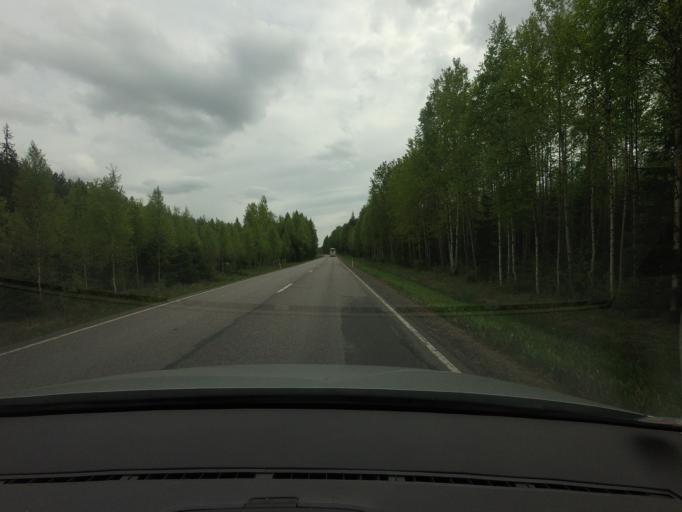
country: FI
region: South Karelia
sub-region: Lappeenranta
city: Taavetti
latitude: 60.8126
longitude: 27.3884
